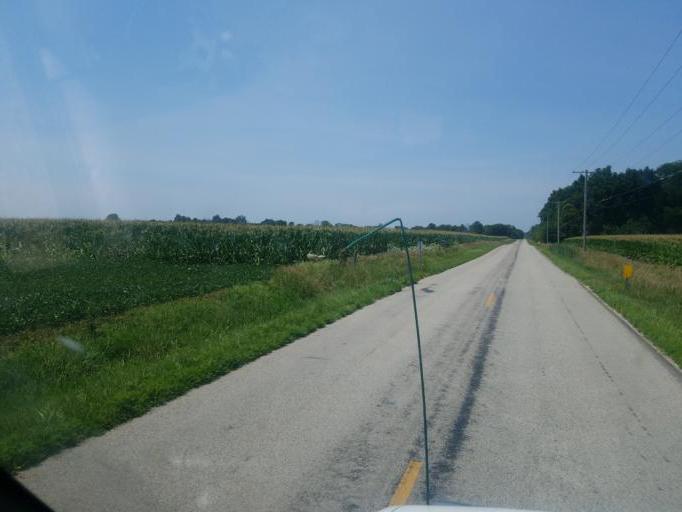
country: US
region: Ohio
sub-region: Shelby County
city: Sidney
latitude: 40.3052
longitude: -84.0935
